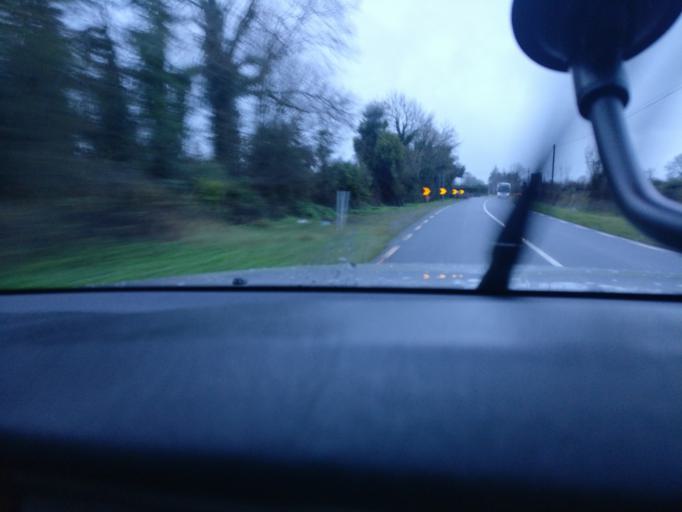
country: IE
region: Connaught
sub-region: County Galway
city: Ballinasloe
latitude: 53.2816
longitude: -8.3689
